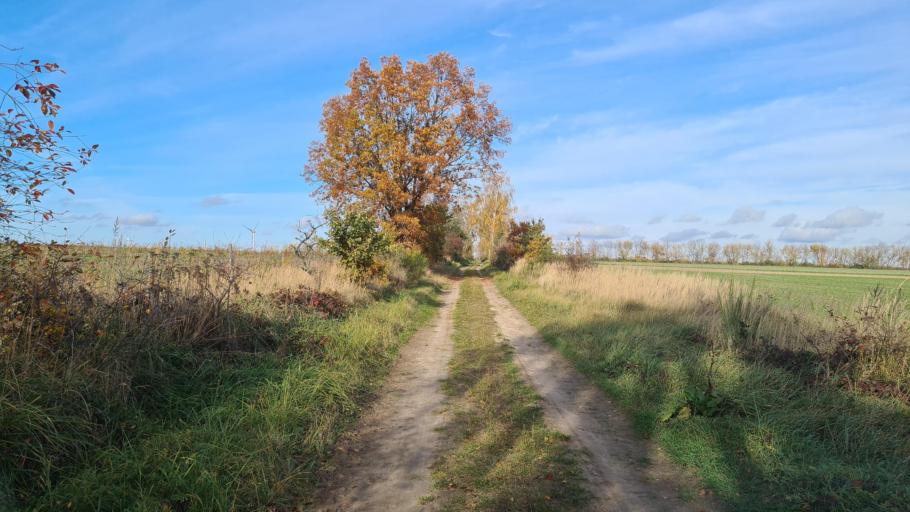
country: DE
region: Saxony-Anhalt
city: Zahna
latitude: 51.9697
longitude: 12.8387
